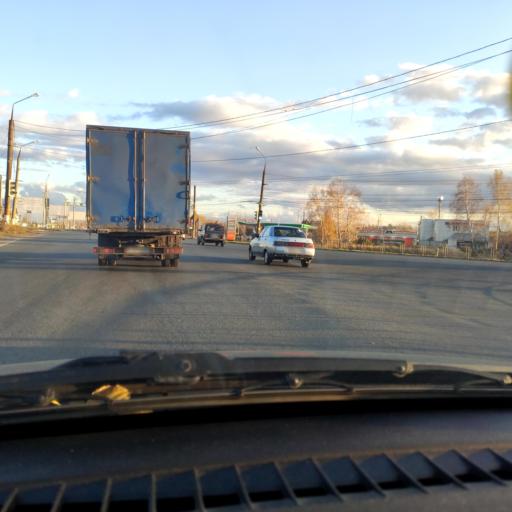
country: RU
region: Samara
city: Tol'yatti
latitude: 53.5456
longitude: 49.3798
